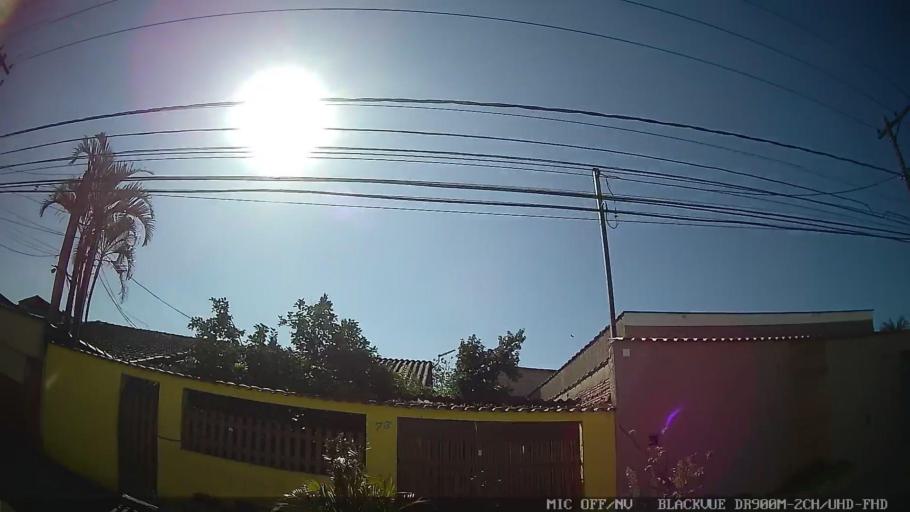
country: BR
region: Sao Paulo
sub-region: Guaruja
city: Guaruja
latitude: -23.9592
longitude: -46.2866
